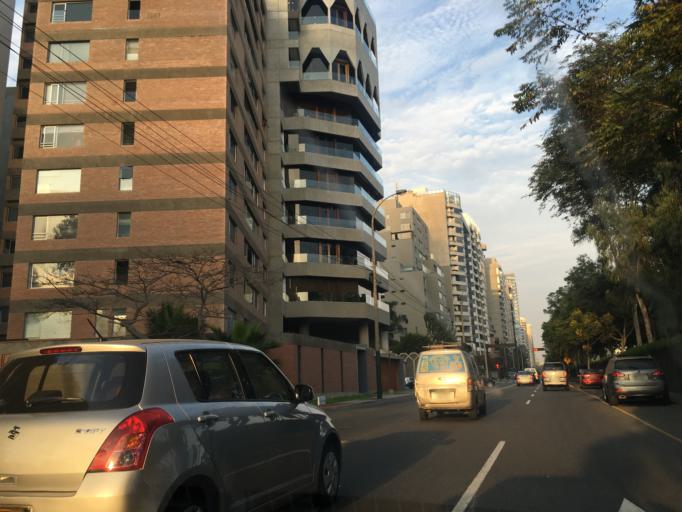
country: PE
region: Lima
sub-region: Lima
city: San Isidro
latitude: -12.0988
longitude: -77.0480
